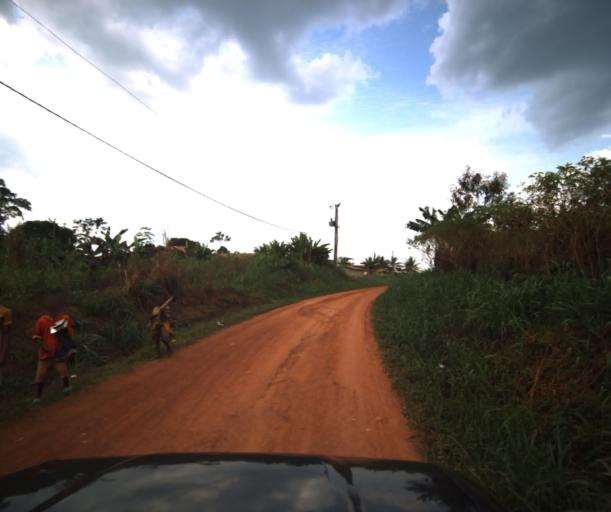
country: CM
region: Centre
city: Akono
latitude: 3.5985
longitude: 11.1786
